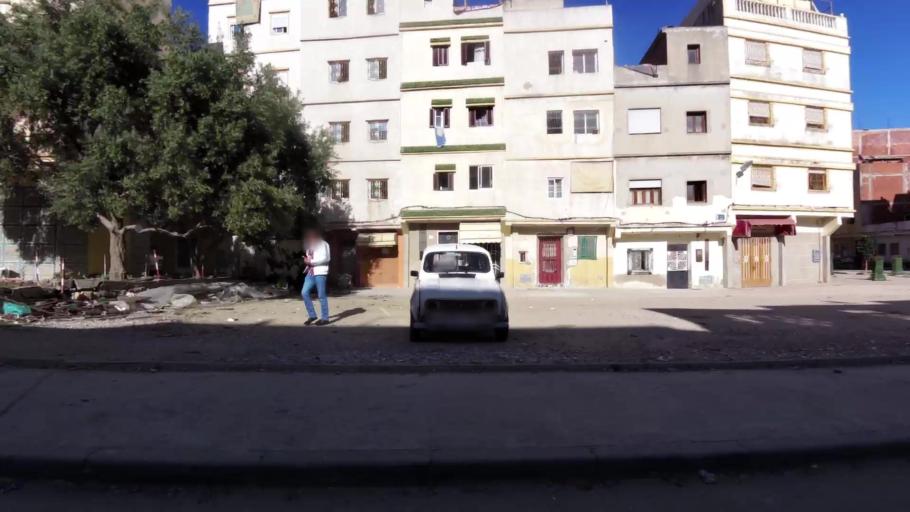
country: MA
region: Tanger-Tetouan
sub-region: Tanger-Assilah
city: Tangier
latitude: 35.7436
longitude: -5.8051
